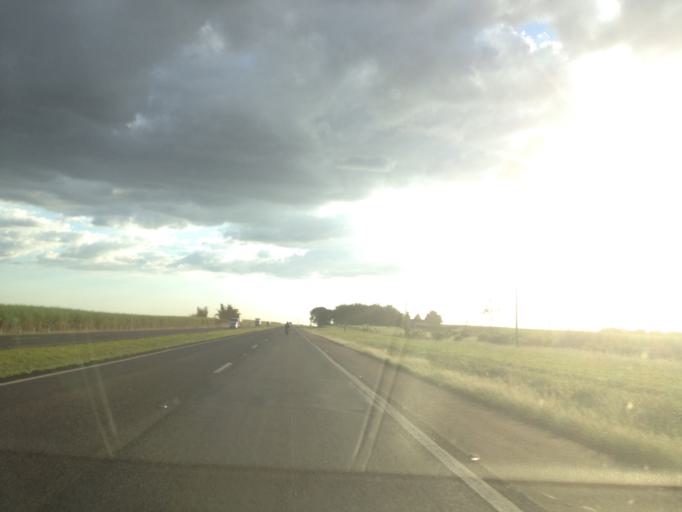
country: BR
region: Sao Paulo
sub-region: Jau
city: Jau
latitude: -22.2698
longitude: -48.4640
